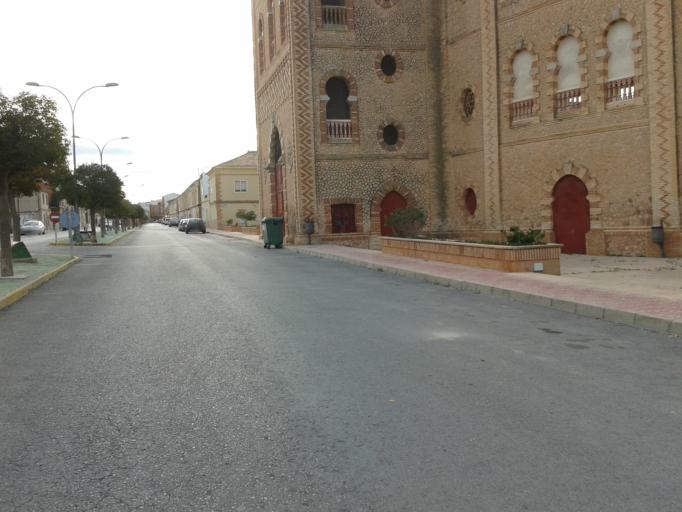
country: ES
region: Castille-La Mancha
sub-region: Provincia de Albacete
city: Caudete
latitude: 38.7114
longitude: -0.9829
